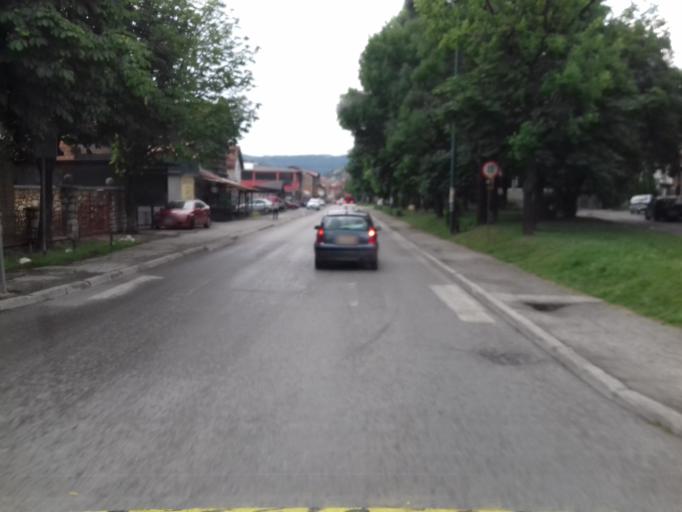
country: BA
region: Federation of Bosnia and Herzegovina
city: Visoko
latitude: 43.9926
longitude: 18.1734
